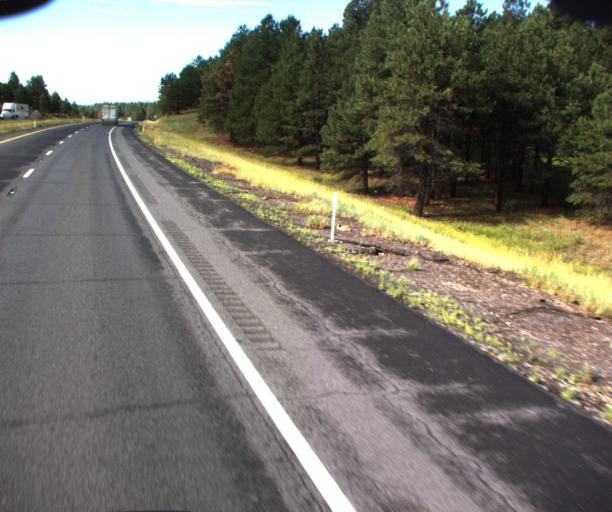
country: US
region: Arizona
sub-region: Coconino County
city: Kachina Village
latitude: 35.1187
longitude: -111.6805
